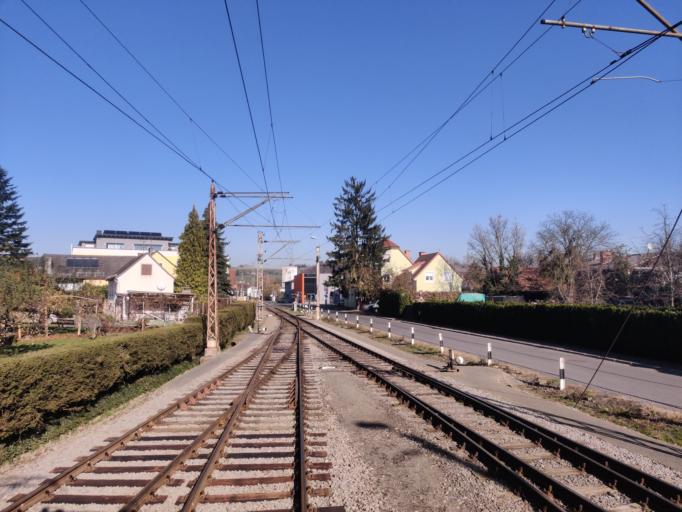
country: AT
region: Styria
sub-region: Politischer Bezirk Suedoststeiermark
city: Feldbach
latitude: 46.9503
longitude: 15.8976
